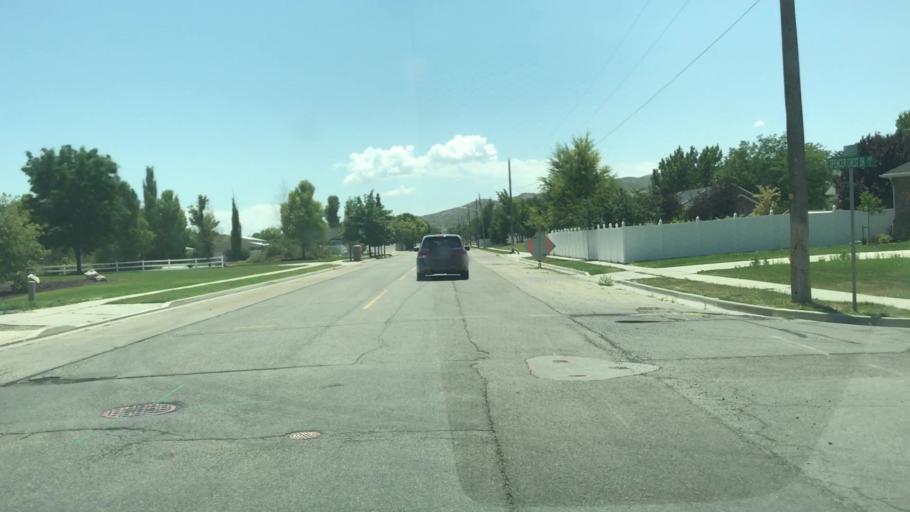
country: US
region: Utah
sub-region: Salt Lake County
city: Bluffdale
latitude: 40.4846
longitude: -111.9484
